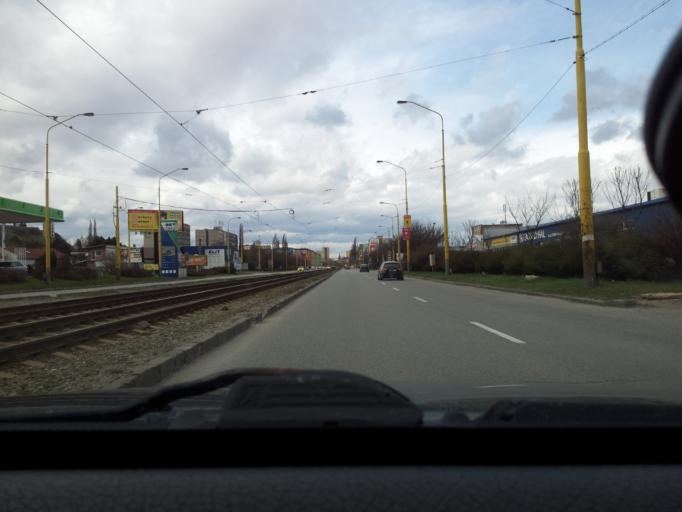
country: SK
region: Kosicky
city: Kosice
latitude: 48.7000
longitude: 21.2634
